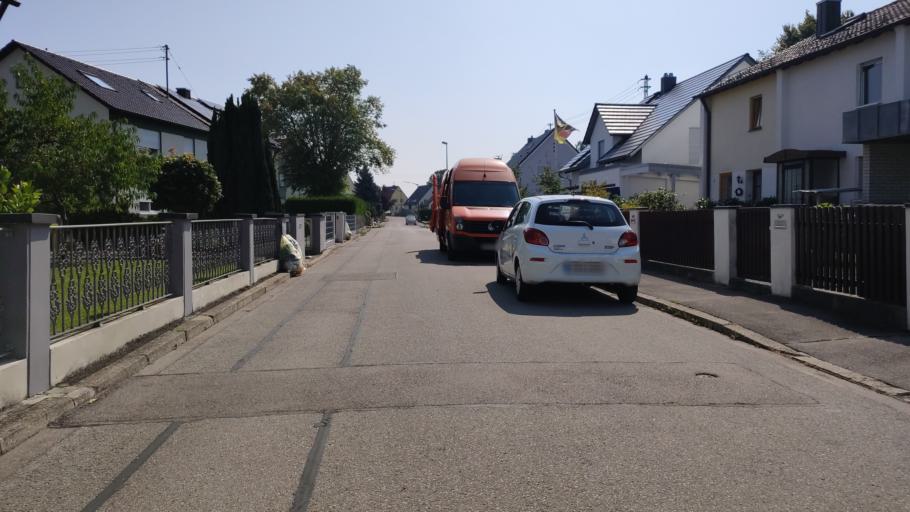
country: DE
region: Bavaria
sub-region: Swabia
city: Bobingen
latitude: 48.2616
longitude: 10.8275
